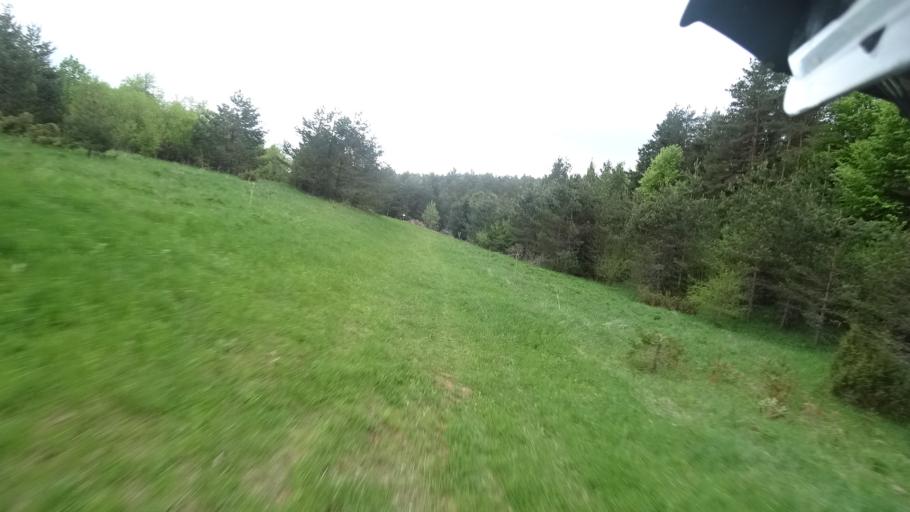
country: HR
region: Licko-Senjska
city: Jezerce
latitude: 44.8771
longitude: 15.4365
